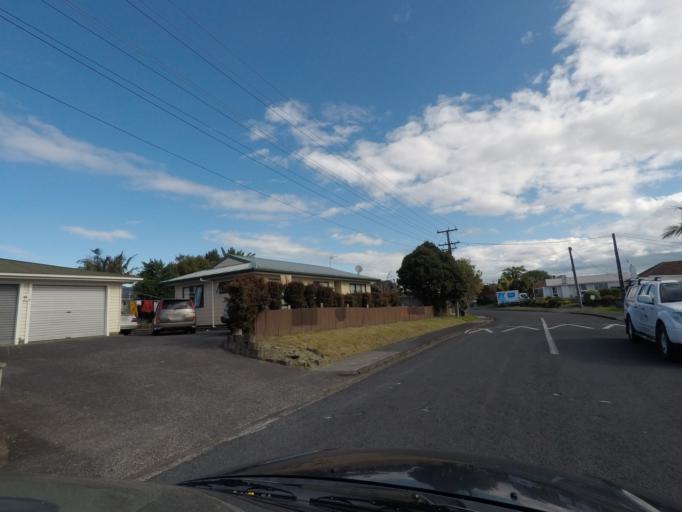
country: NZ
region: Auckland
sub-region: Auckland
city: Rosebank
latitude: -36.8693
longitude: 174.6425
